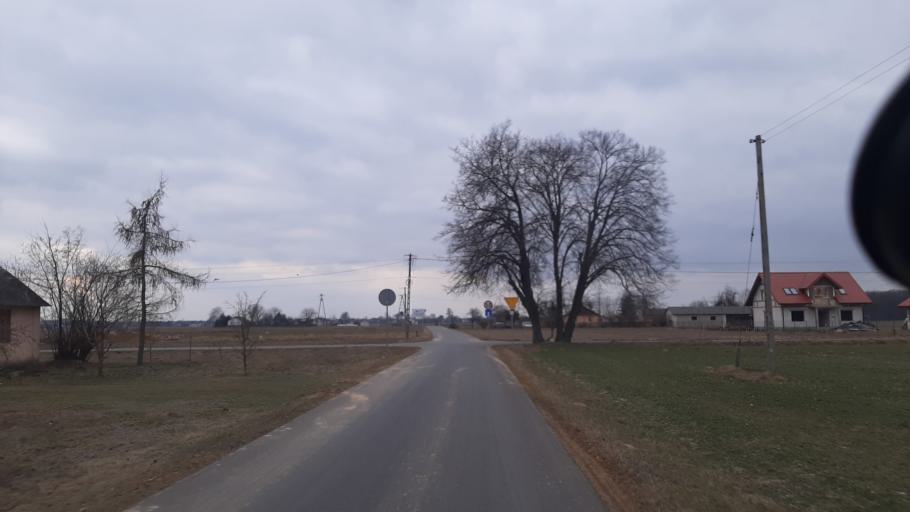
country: PL
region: Lublin Voivodeship
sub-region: Powiat lubelski
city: Garbow
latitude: 51.3649
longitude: 22.3985
